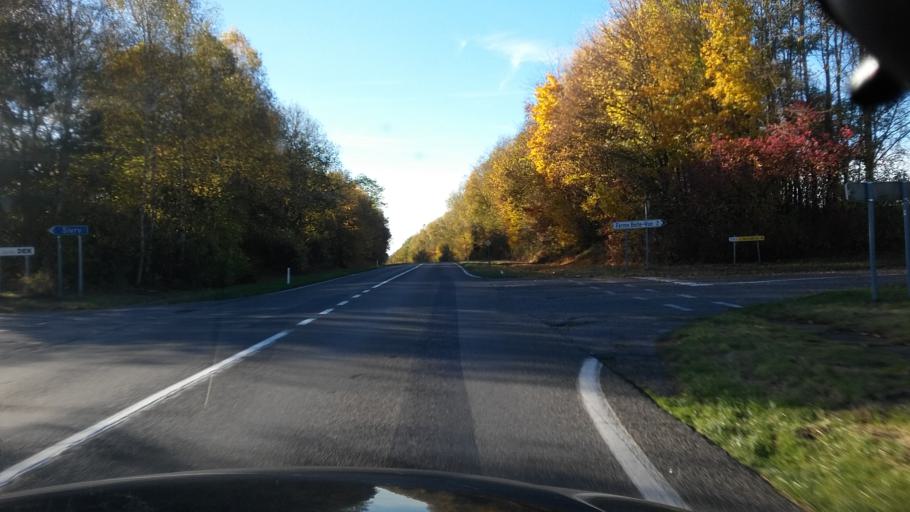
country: BE
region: Wallonia
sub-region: Province du Luxembourg
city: Etalle
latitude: 49.6757
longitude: 5.6195
